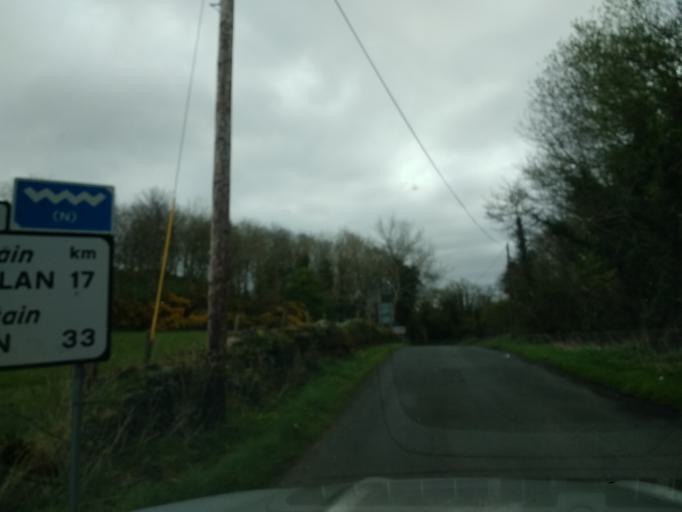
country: IE
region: Ulster
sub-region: County Donegal
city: Ramelton
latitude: 55.1946
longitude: -7.6377
